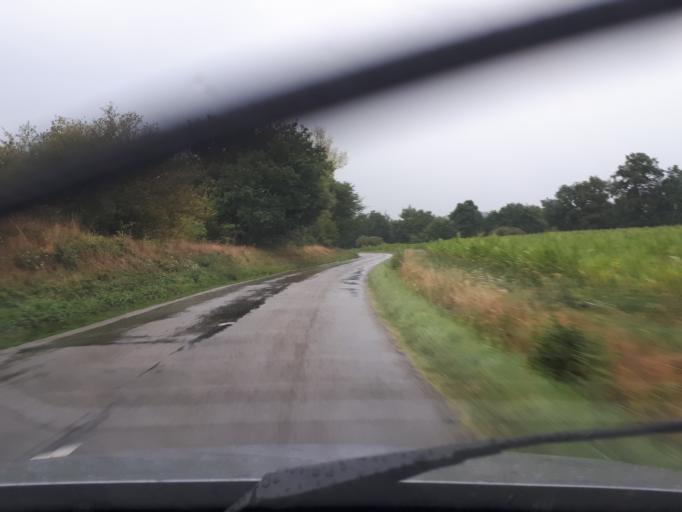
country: FR
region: Rhone-Alpes
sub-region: Departement de la Loire
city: Feurs
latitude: 45.7152
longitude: 4.2779
